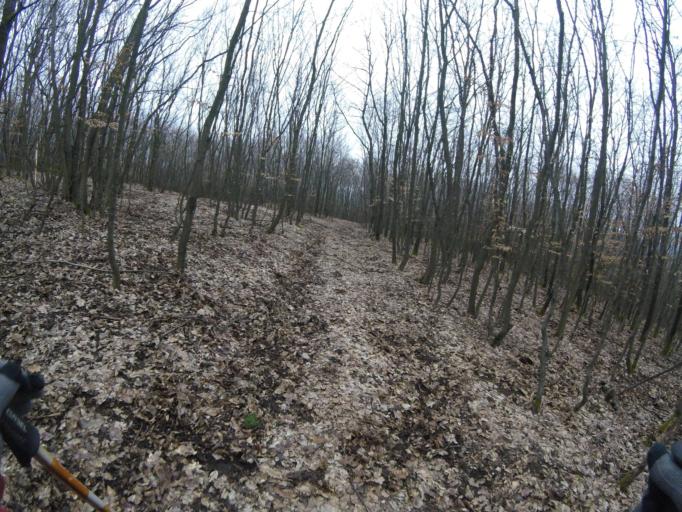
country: HU
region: Borsod-Abauj-Zemplen
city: Rudabanya
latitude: 48.4604
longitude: 20.6138
